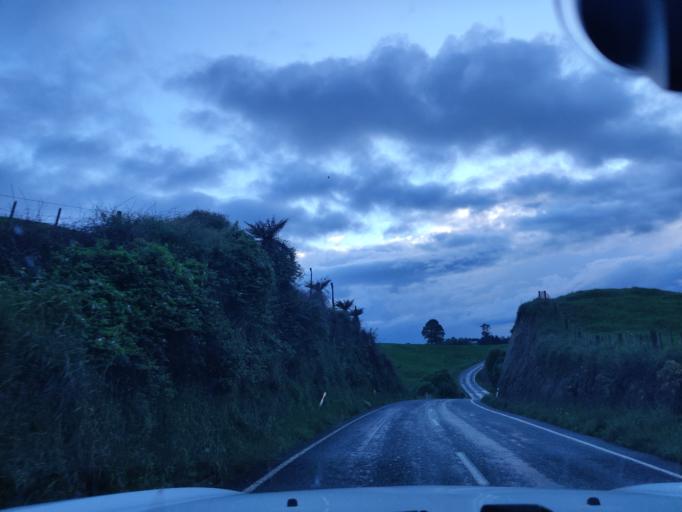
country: NZ
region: Waikato
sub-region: South Waikato District
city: Tokoroa
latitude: -38.1859
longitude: 175.7910
